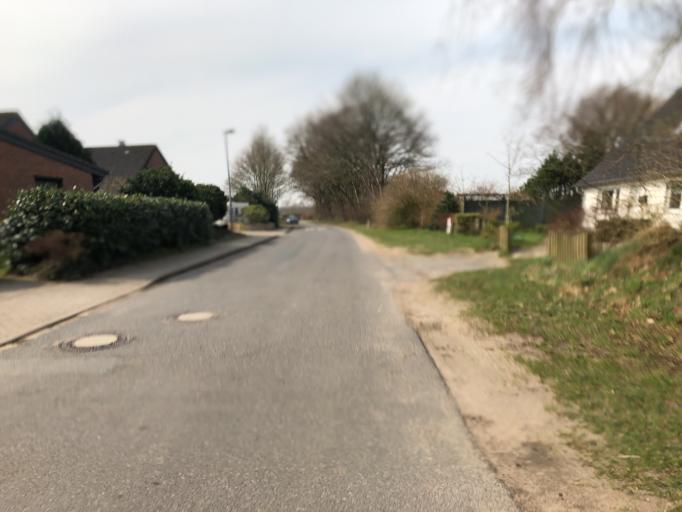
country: DE
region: Schleswig-Holstein
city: Wanderup
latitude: 54.6846
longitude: 9.3205
